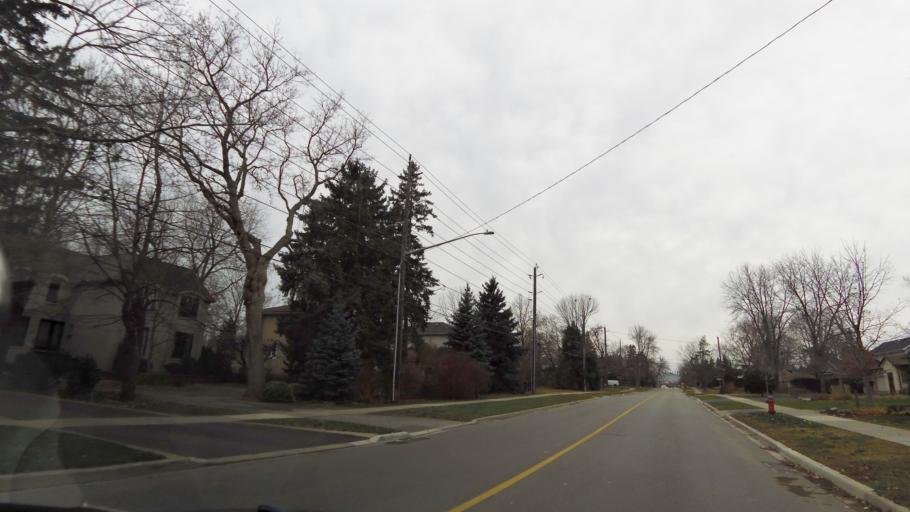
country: CA
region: Ontario
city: Oakville
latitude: 43.4765
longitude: -79.6539
